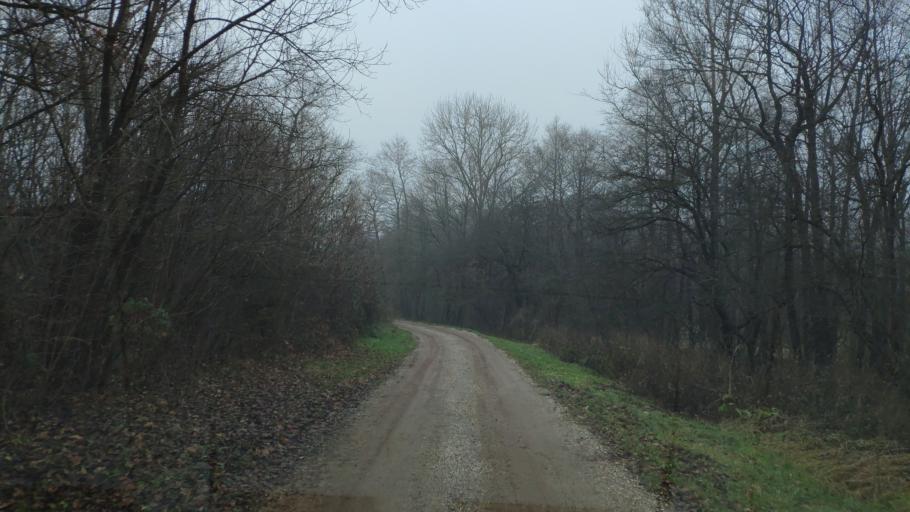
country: SK
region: Banskobystricky
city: Revuca
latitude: 48.6496
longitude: 20.2581
